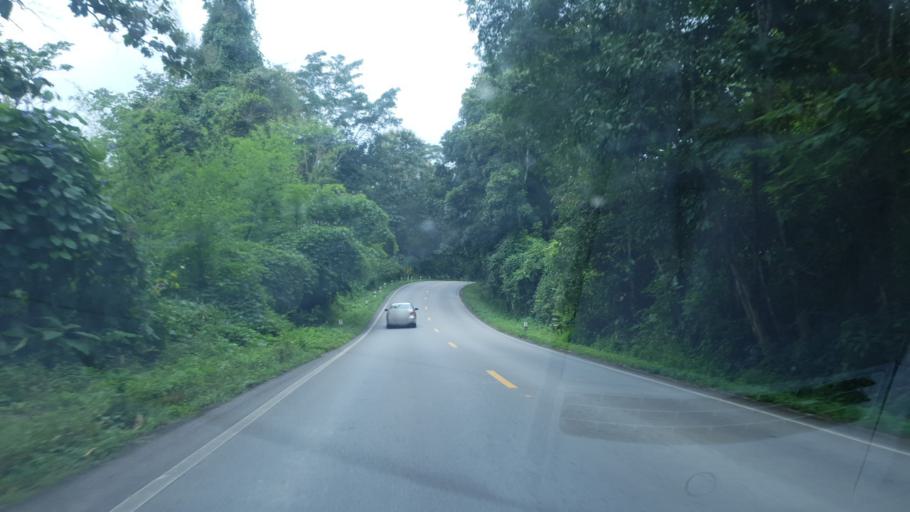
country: TH
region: Mae Hong Son
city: Khun Yuam
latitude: 18.7138
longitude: 97.9097
